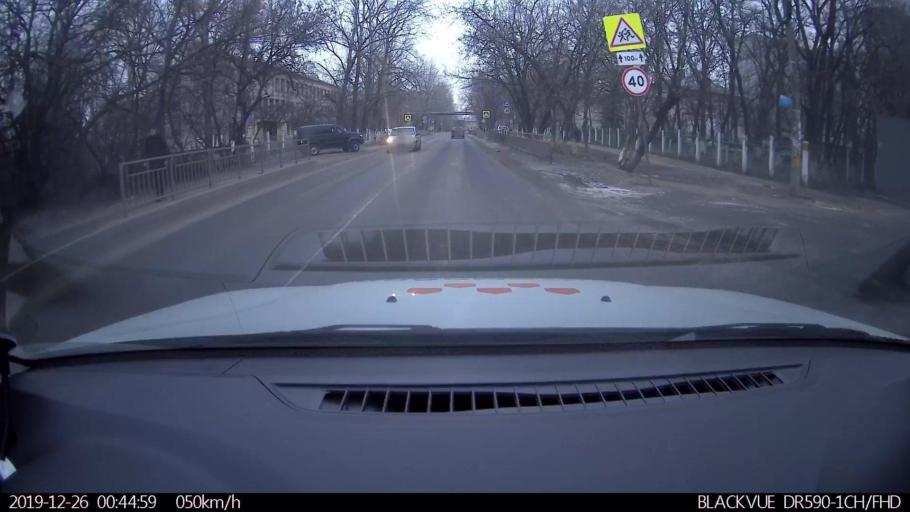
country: RU
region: Nizjnij Novgorod
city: Nizhniy Novgorod
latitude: 56.3021
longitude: 43.8794
